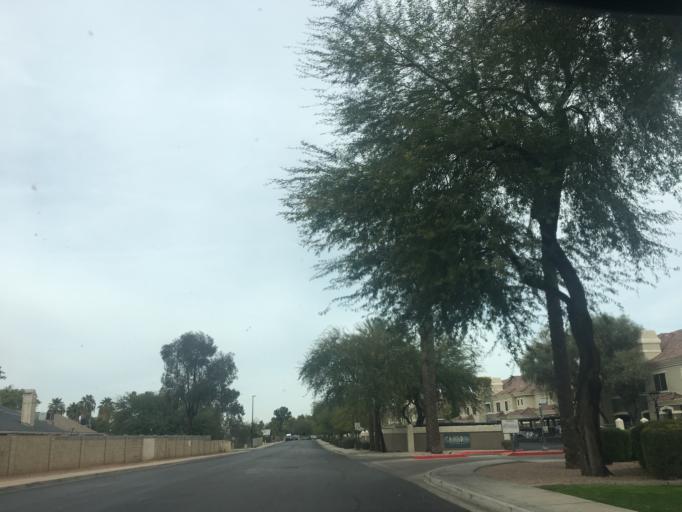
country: US
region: Arizona
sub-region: Maricopa County
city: Gilbert
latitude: 33.3647
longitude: -111.7932
